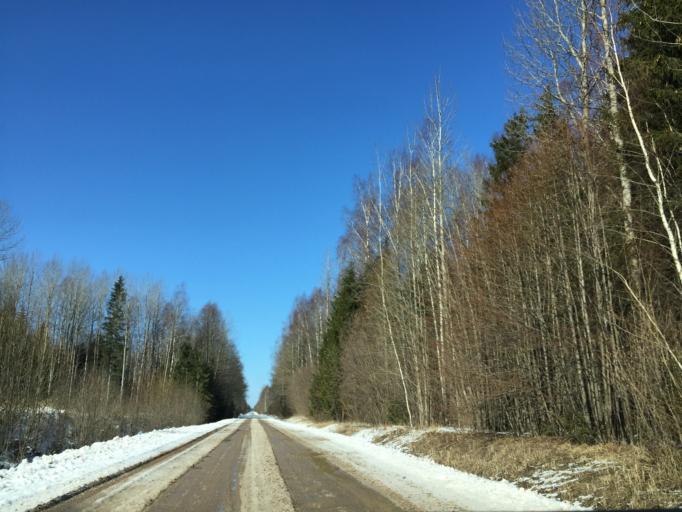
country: LV
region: Salacgrivas
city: Ainazi
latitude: 58.0279
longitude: 24.5540
